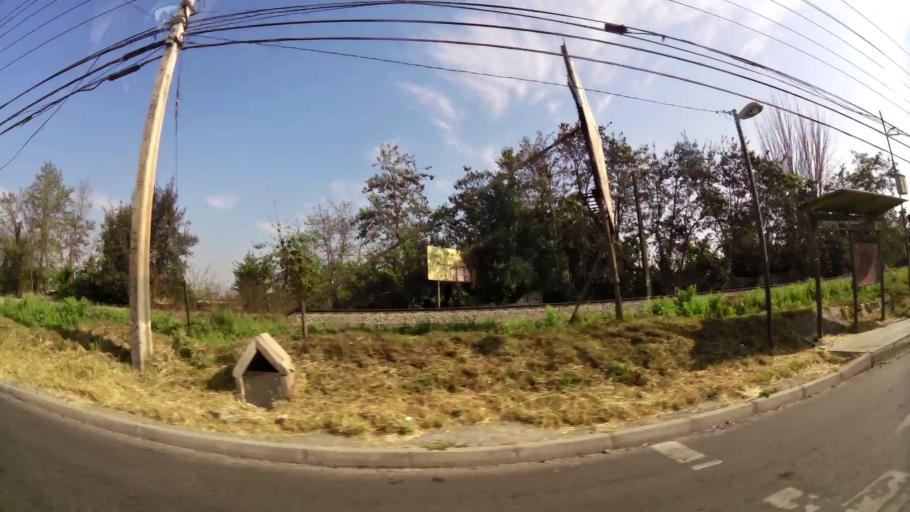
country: CL
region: Santiago Metropolitan
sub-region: Provincia de Talagante
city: Penaflor
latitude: -33.5513
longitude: -70.7919
